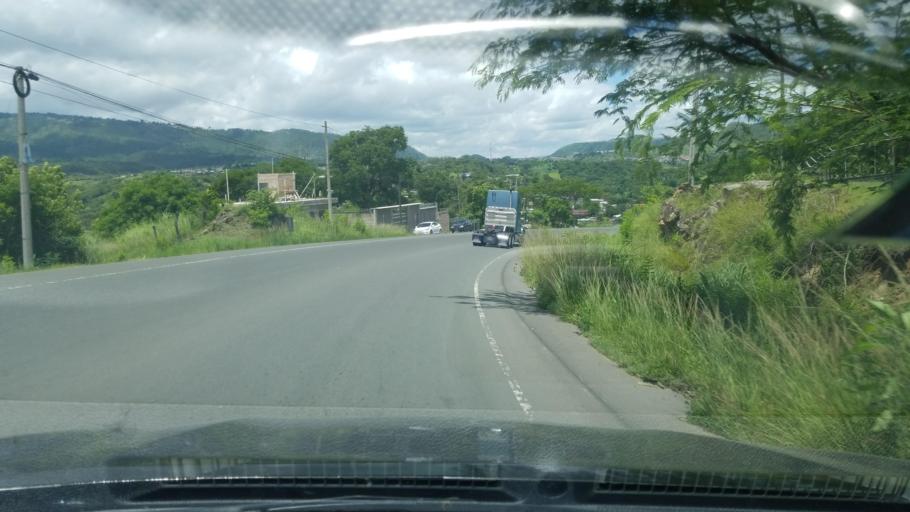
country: HN
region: Francisco Morazan
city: Rio Abajo
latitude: 14.1764
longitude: -87.2040
